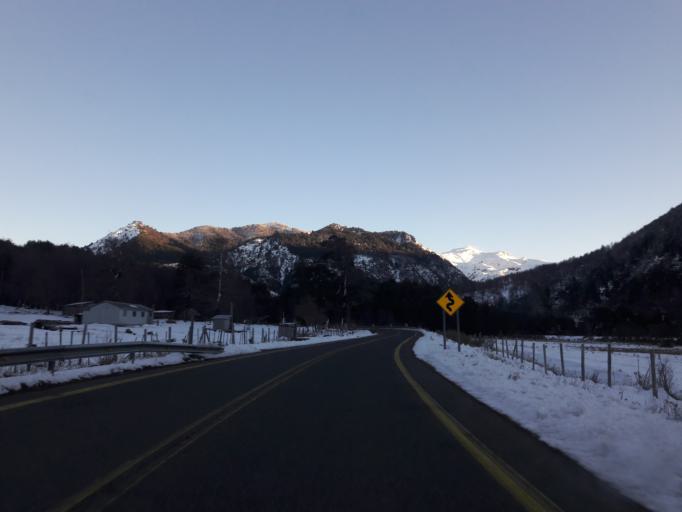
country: CL
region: Araucania
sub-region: Provincia de Cautin
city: Vilcun
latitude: -38.5005
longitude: -71.5195
